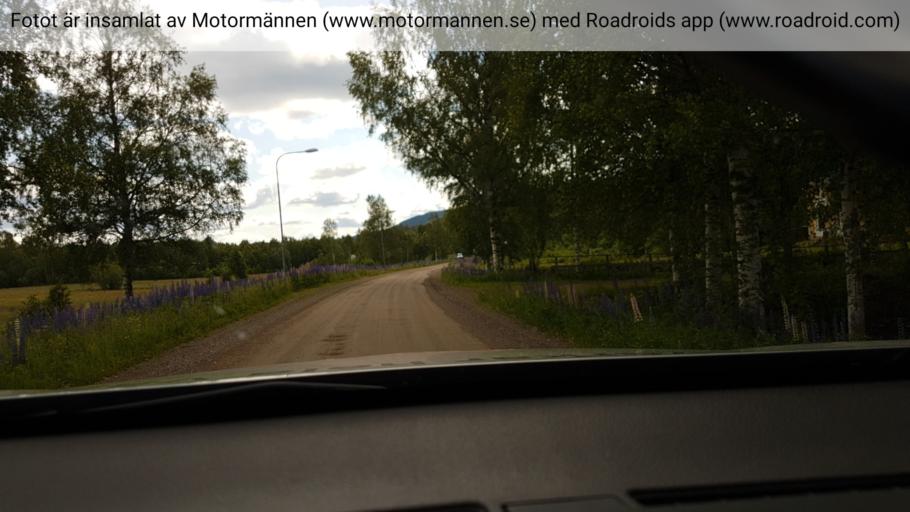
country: SE
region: Vaermland
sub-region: Hagfors Kommun
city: Ekshaerad
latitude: 60.3939
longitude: 13.2752
